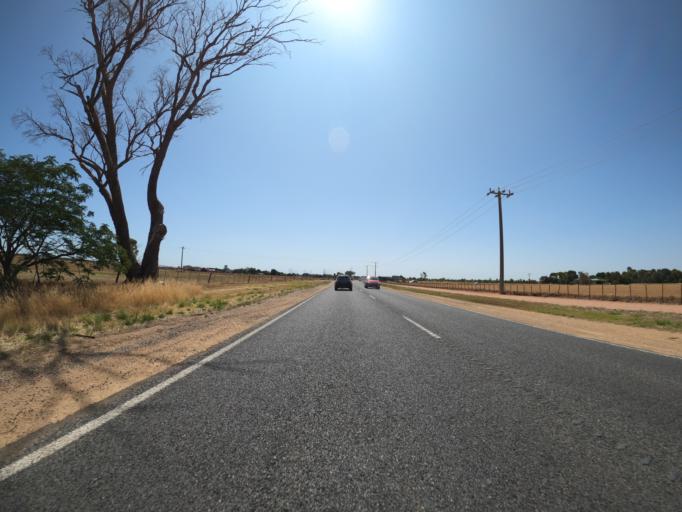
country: AU
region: Victoria
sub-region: Moira
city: Yarrawonga
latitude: -36.0181
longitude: 146.0505
